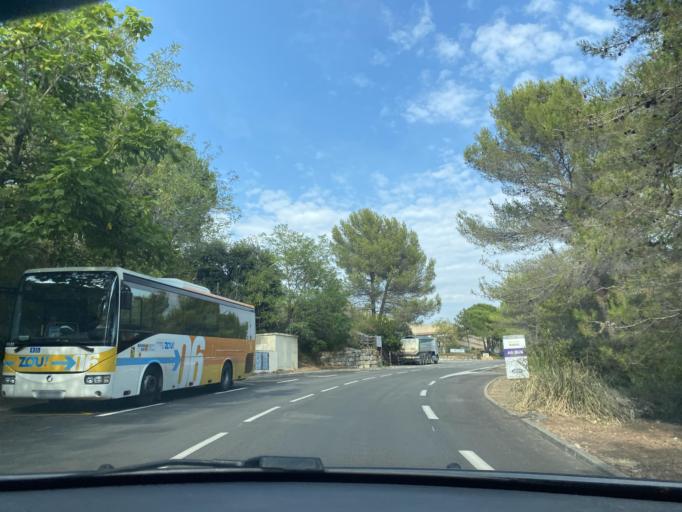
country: FR
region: Provence-Alpes-Cote d'Azur
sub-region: Departement des Alpes-Maritimes
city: Biot
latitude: 43.6271
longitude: 7.0485
